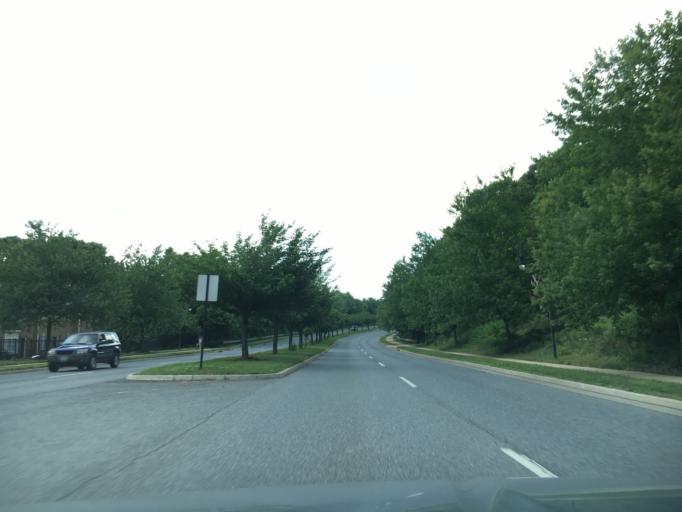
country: US
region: Virginia
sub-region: Campbell County
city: Timberlake
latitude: 37.3491
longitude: -79.2424
